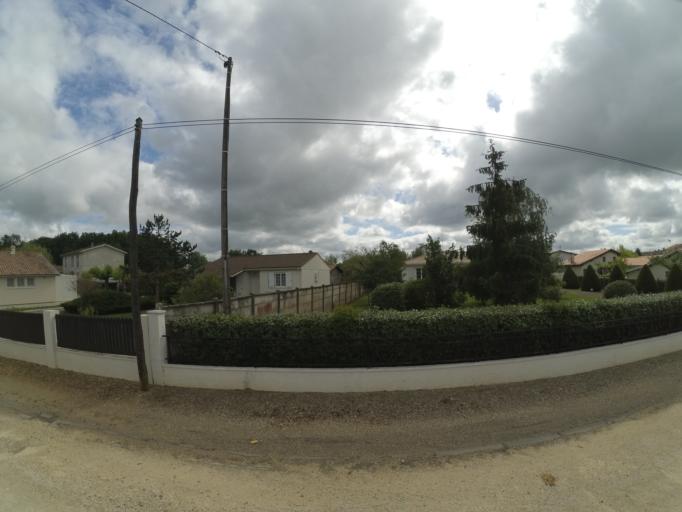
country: FR
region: Aquitaine
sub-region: Departement de la Gironde
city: Macau
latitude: 45.0076
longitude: -0.6106
